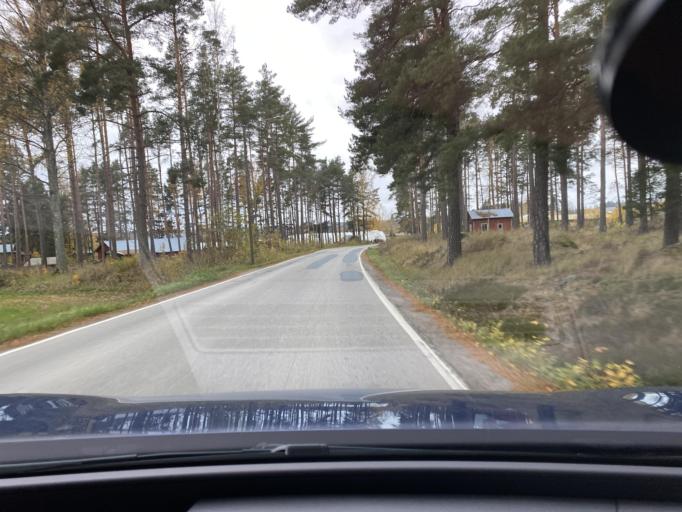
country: FI
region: Varsinais-Suomi
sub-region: Vakka-Suomi
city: Laitila
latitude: 60.9231
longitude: 21.6054
